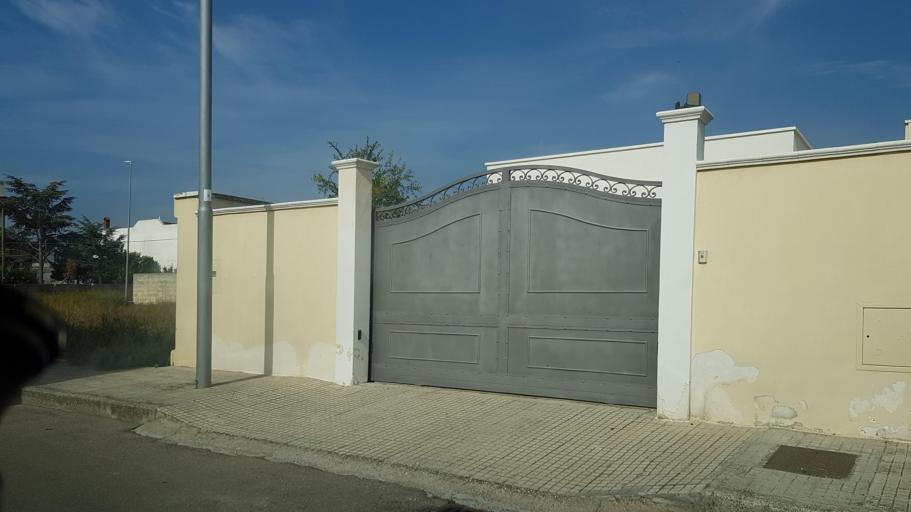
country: IT
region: Apulia
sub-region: Provincia di Brindisi
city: San Donaci
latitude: 40.4475
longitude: 17.9281
